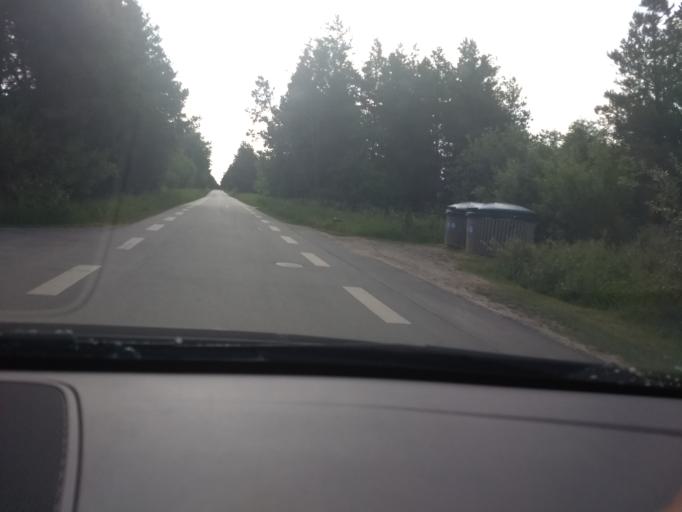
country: DE
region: Schleswig-Holstein
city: List
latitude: 55.1296
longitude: 8.5300
